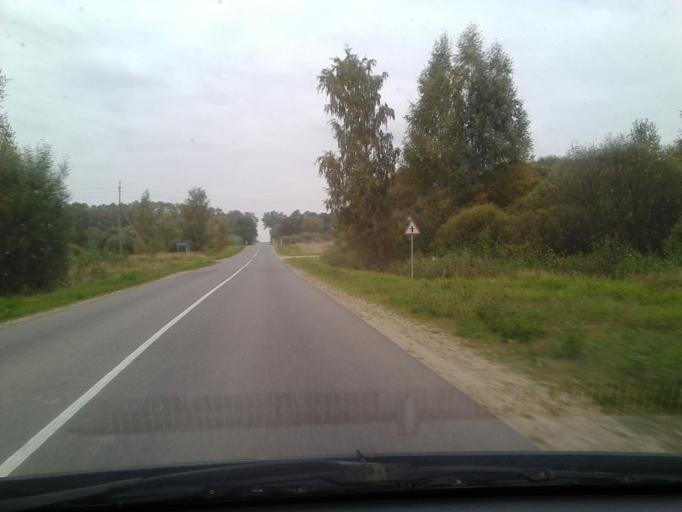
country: BY
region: Vitebsk
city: Pastavy
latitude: 55.1266
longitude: 26.9333
